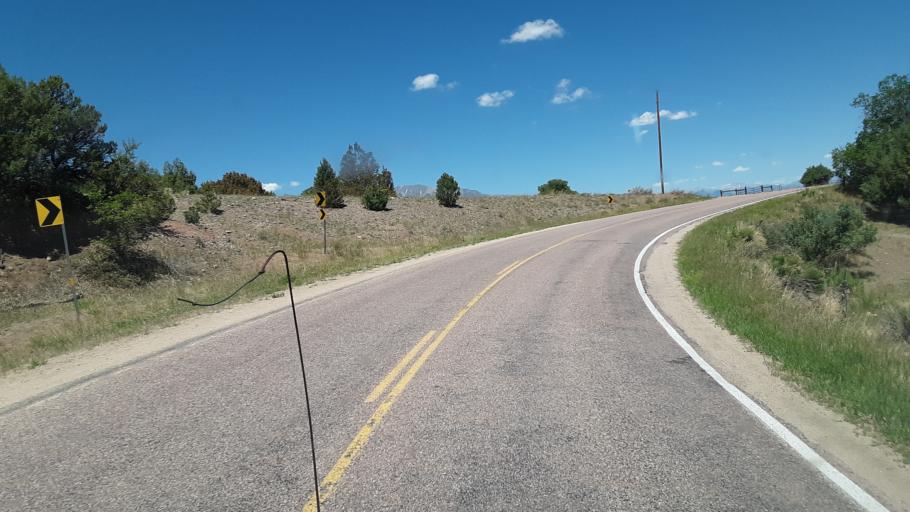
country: US
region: Colorado
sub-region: Custer County
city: Westcliffe
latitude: 38.3124
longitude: -105.6579
